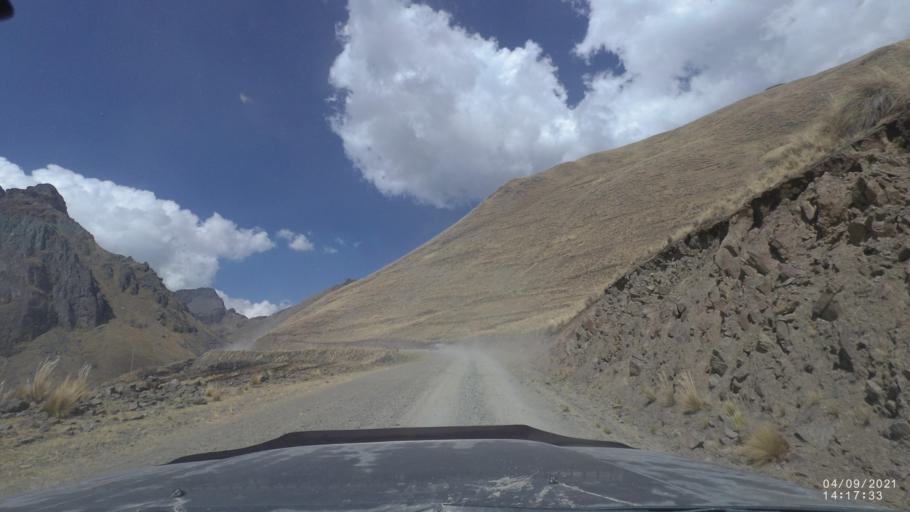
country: BO
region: Cochabamba
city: Sipe Sipe
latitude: -17.2304
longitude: -66.4342
